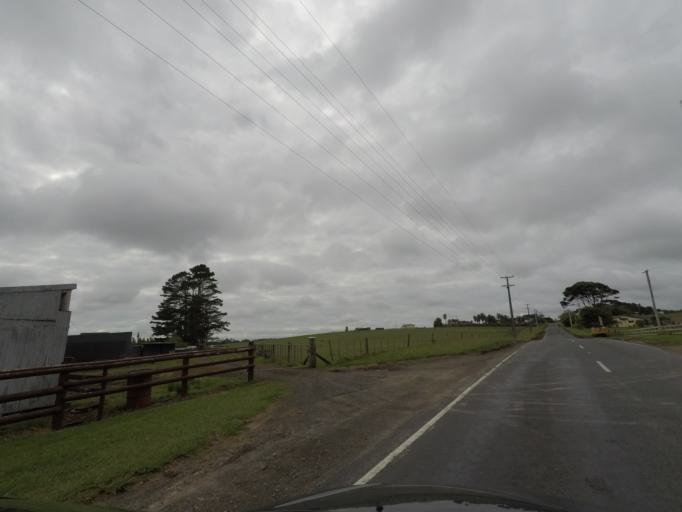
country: NZ
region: Auckland
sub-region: Auckland
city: Rosebank
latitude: -36.8078
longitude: 174.5763
